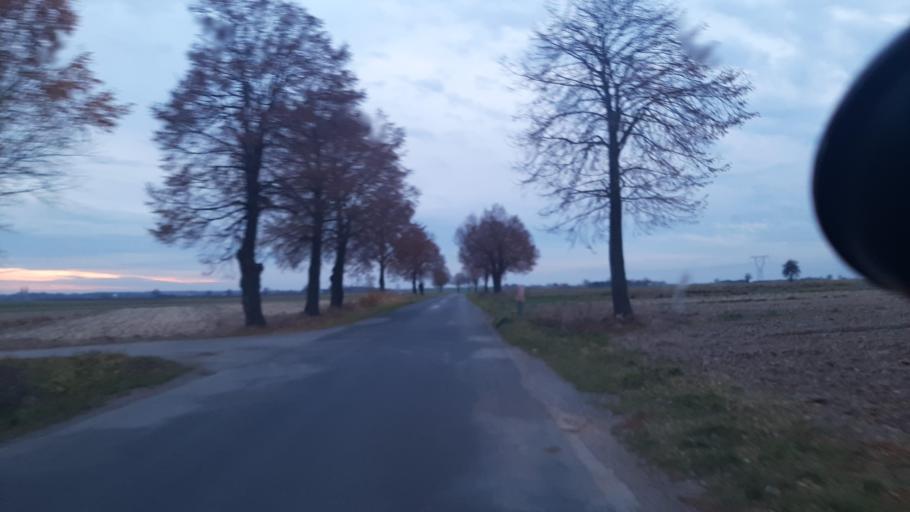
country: PL
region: Lublin Voivodeship
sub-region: Powiat lubelski
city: Garbow
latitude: 51.3773
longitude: 22.3701
